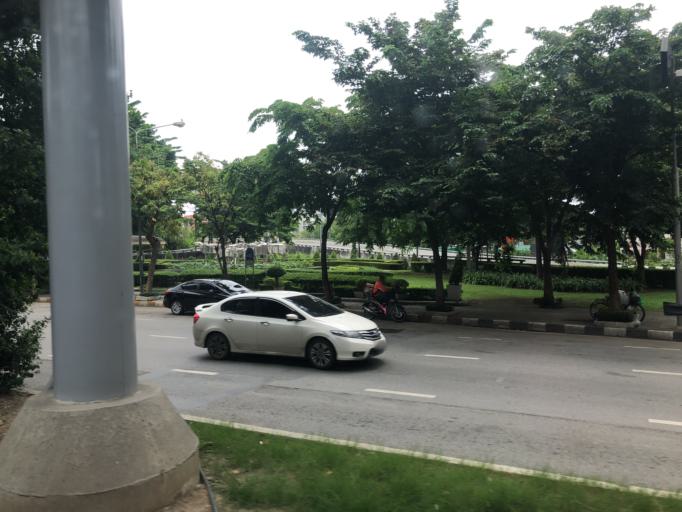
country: TH
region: Bangkok
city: Phra Khanong
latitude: 13.6753
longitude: 100.6077
